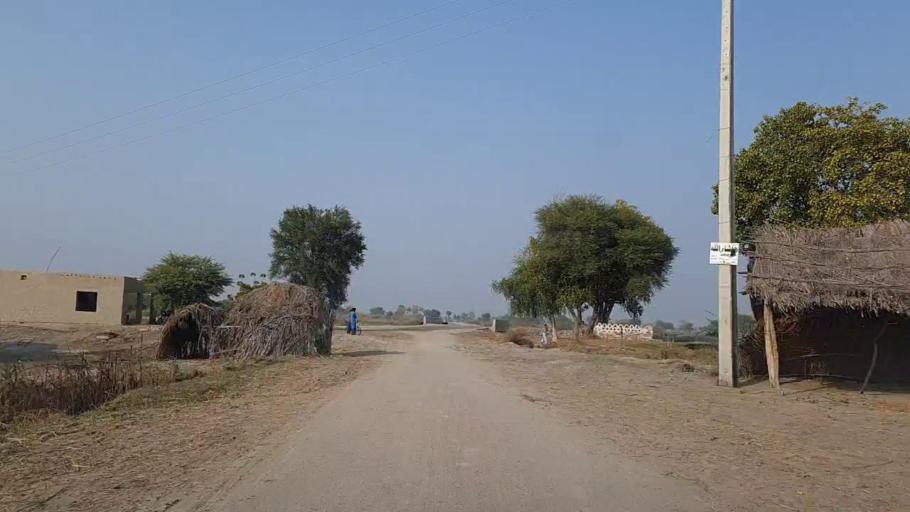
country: PK
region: Sindh
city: Nawabshah
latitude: 26.3422
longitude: 68.4893
